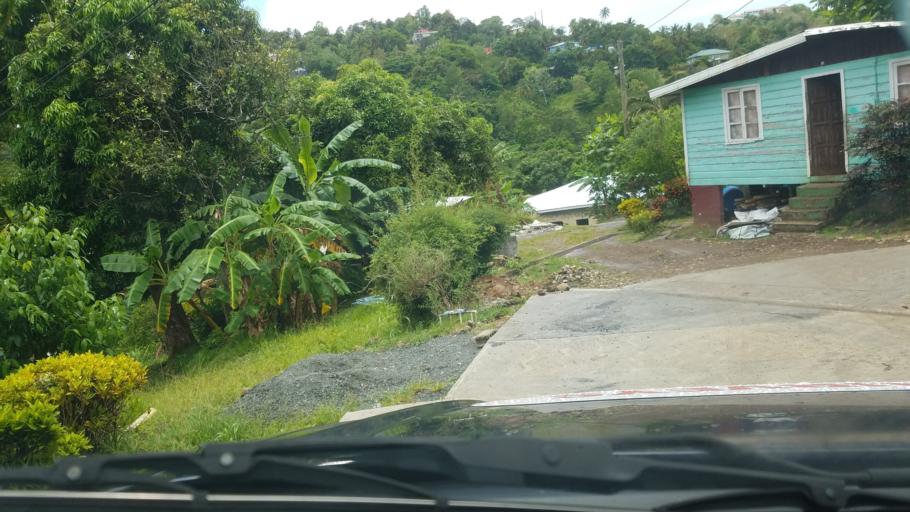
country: LC
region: Castries Quarter
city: Bisee
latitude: 14.0000
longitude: -60.9626
